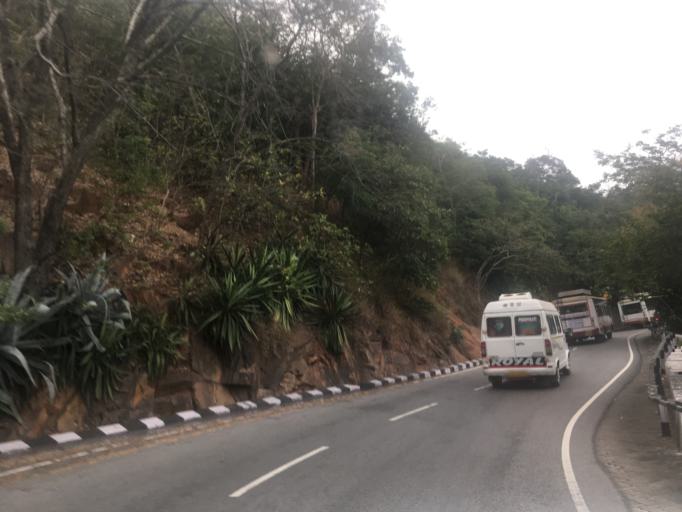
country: IN
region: Andhra Pradesh
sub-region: Chittoor
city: Tirumala
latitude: 13.6665
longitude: 79.3486
